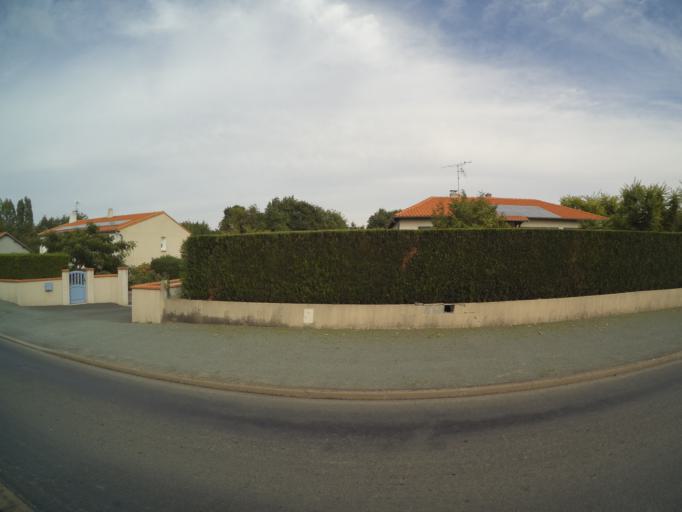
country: FR
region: Pays de la Loire
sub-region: Departement de Maine-et-Loire
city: Saint-Lambert-du-Lattay
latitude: 47.2158
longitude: -0.6021
